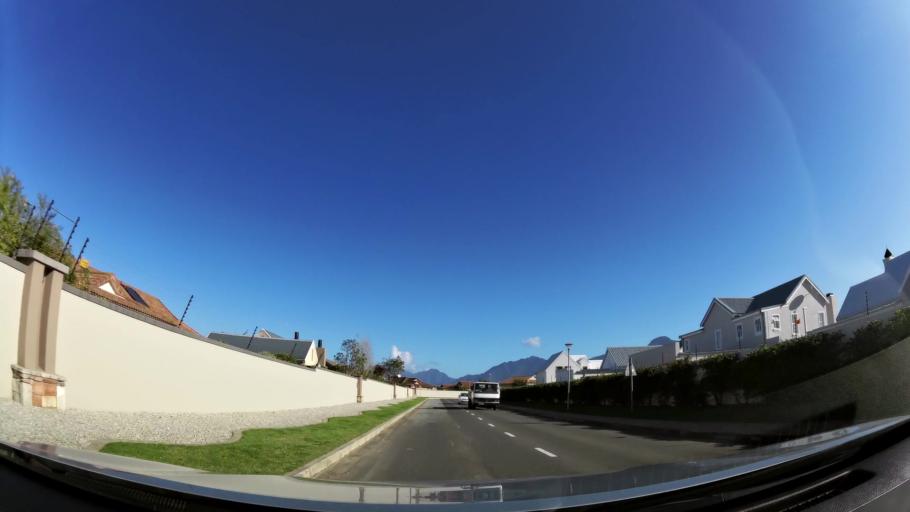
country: ZA
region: Western Cape
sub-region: Eden District Municipality
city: George
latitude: -33.9622
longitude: 22.4281
